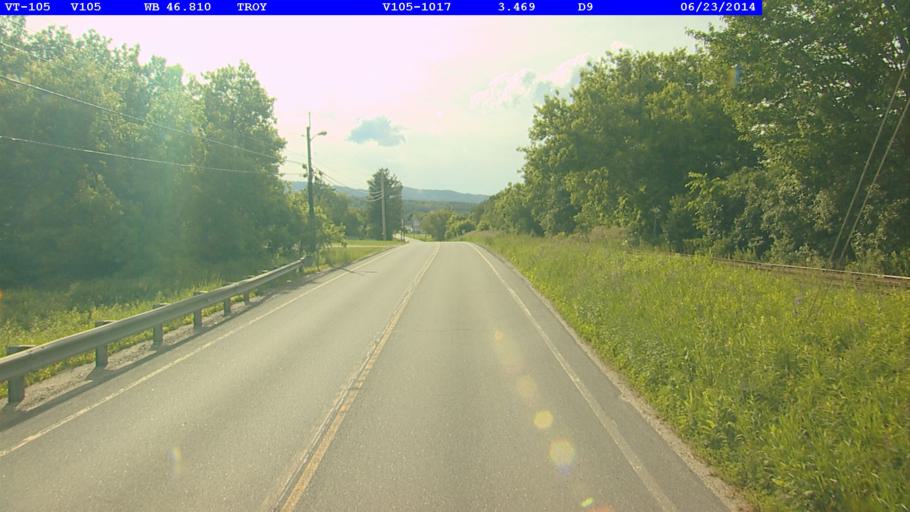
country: US
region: Vermont
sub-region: Orleans County
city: Newport
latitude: 44.9930
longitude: -72.3882
